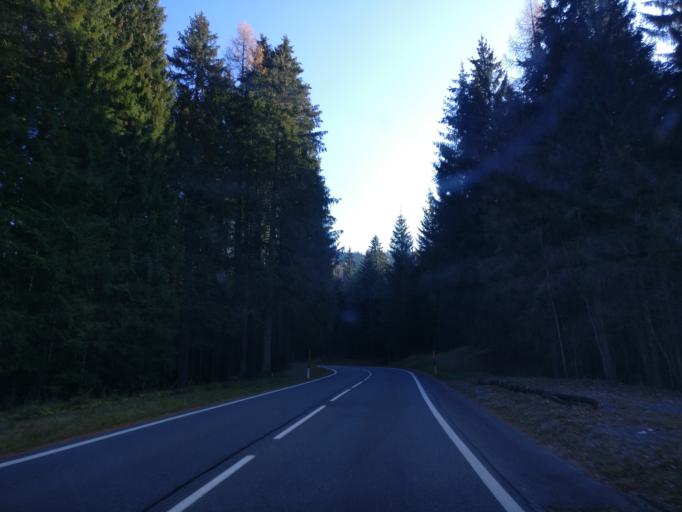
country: AT
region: Salzburg
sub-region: Politischer Bezirk Zell am See
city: Dienten am Hochkonig
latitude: 47.4066
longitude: 12.9835
